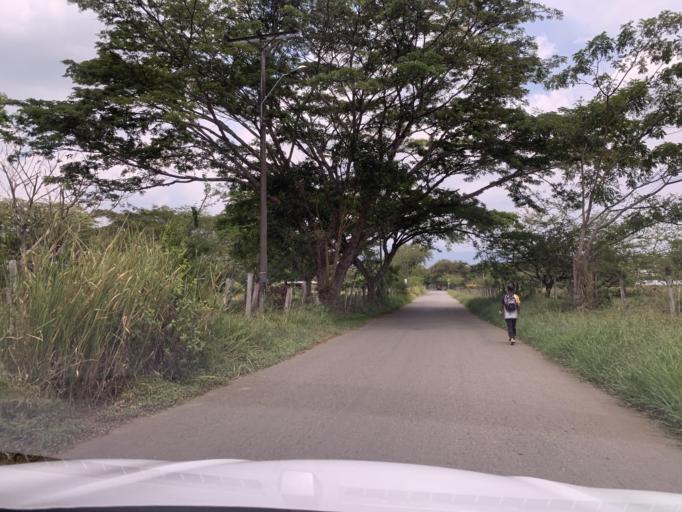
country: CO
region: Valle del Cauca
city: Jamundi
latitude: 3.3097
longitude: -76.5374
